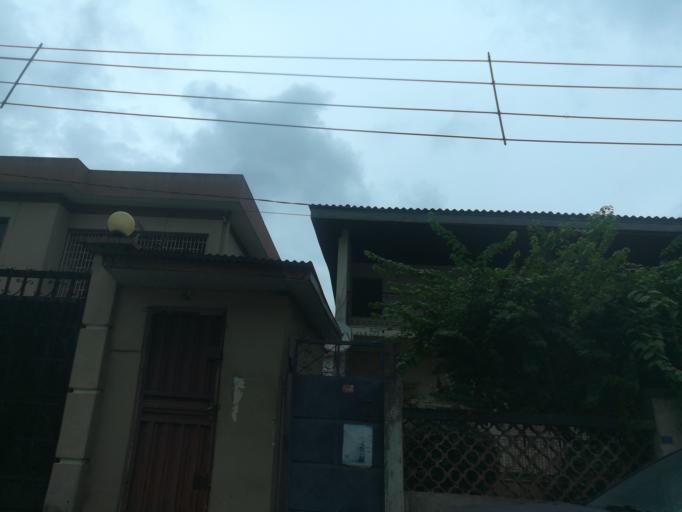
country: NG
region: Lagos
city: Ikeja
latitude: 6.6123
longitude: 3.3471
